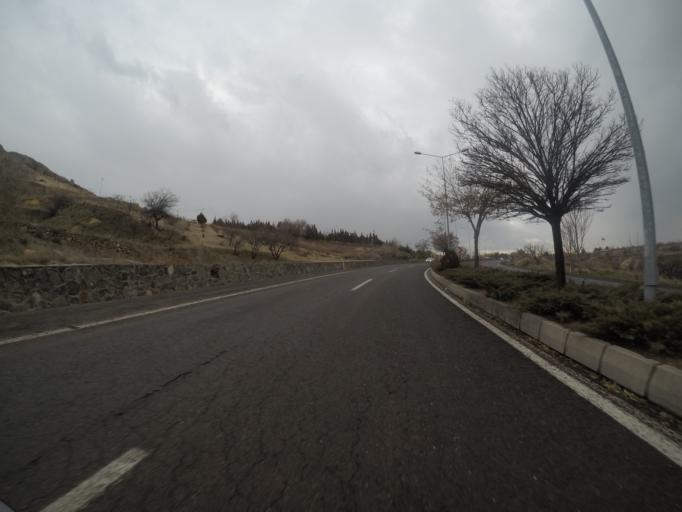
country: TR
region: Nevsehir
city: Urgub
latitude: 38.6369
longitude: 34.9008
